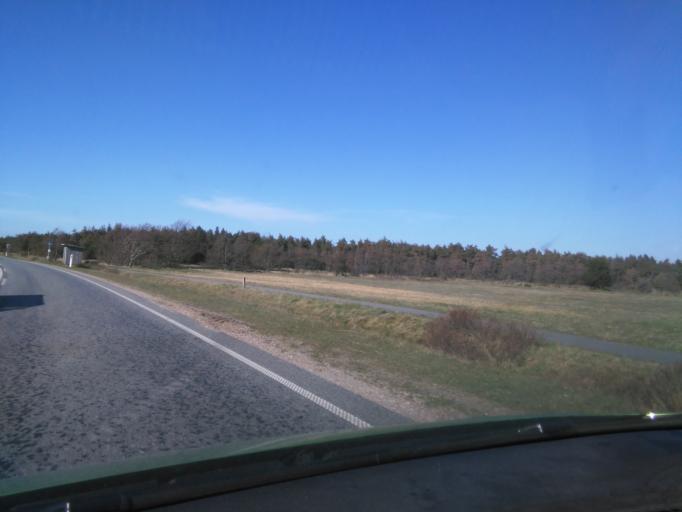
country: DK
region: South Denmark
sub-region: Varde Kommune
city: Oksbol
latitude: 55.5930
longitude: 8.2269
